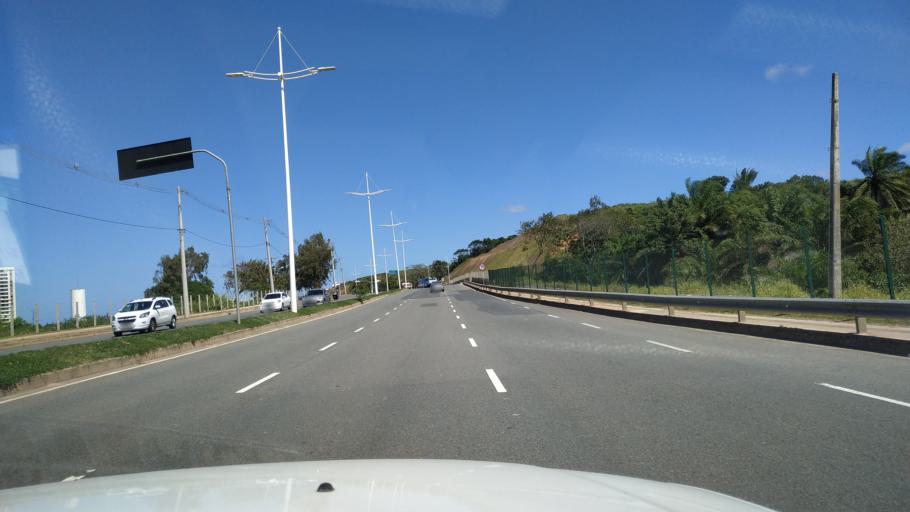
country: BR
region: Bahia
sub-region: Lauro De Freitas
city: Lauro de Freitas
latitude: -12.9322
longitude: -38.3830
